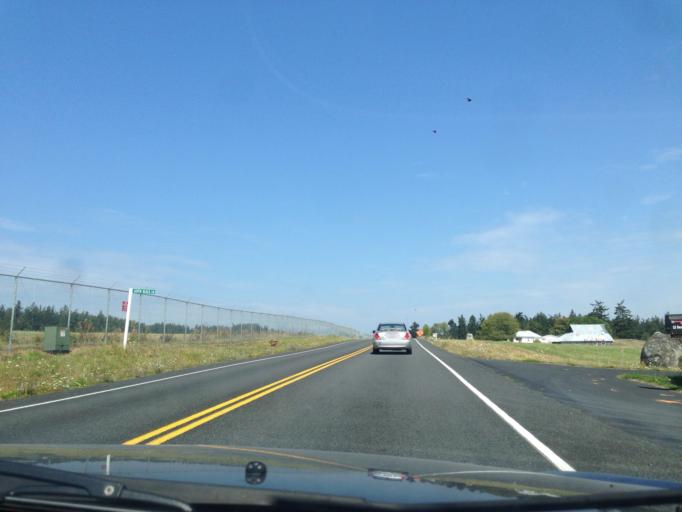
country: US
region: Washington
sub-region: San Juan County
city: Friday Harbor
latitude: 48.5178
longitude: -123.0231
